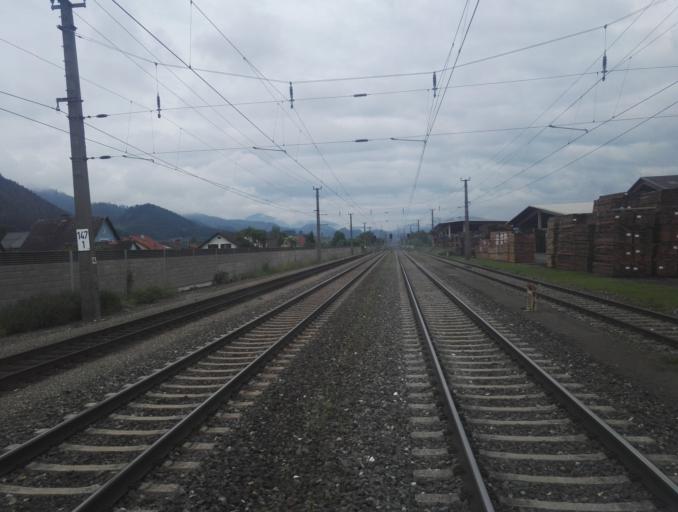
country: AT
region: Styria
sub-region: Politischer Bezirk Bruck-Muerzzuschlag
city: Sankt Marein im Muerztal
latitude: 47.4714
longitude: 15.3686
